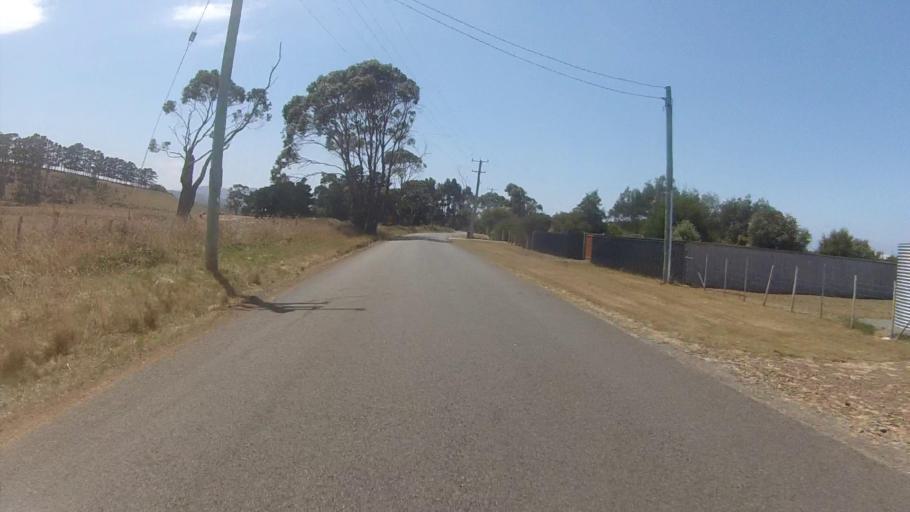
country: AU
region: Tasmania
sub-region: Sorell
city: Sorell
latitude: -42.8276
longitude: 147.8586
